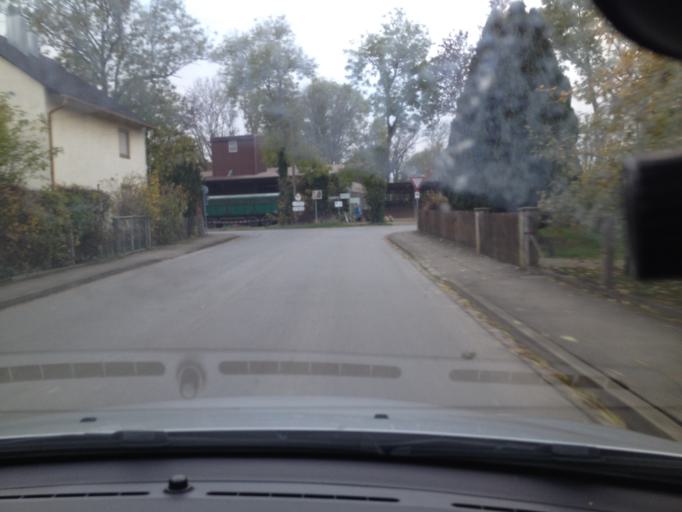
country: DE
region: Bavaria
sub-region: Swabia
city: Kleinaitingen
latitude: 48.2220
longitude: 10.8437
